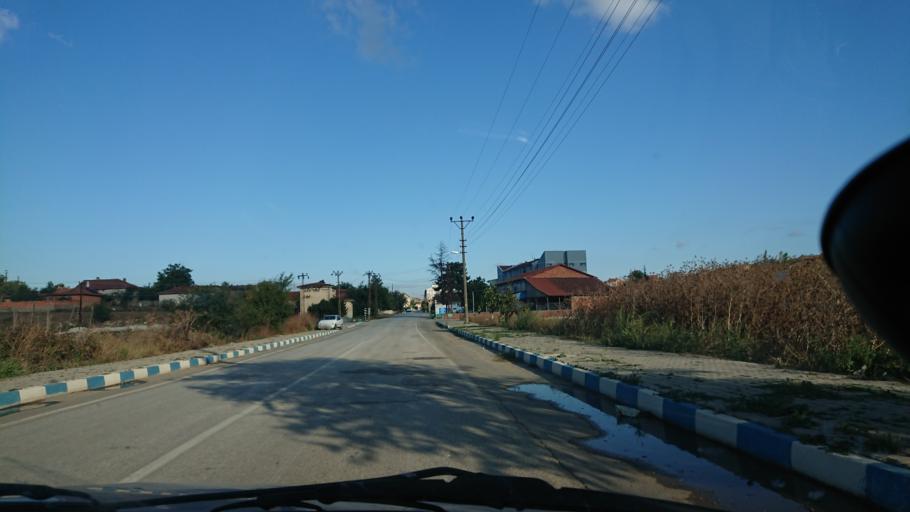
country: TR
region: Bilecik
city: Pazaryeri
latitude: 39.9990
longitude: 29.8911
